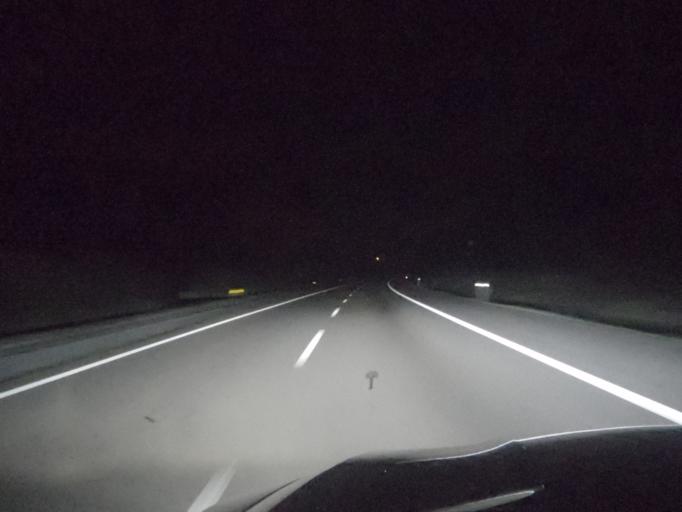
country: PT
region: Aveiro
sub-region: Oliveira do Bairro
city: Oia
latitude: 40.5172
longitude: -8.5465
